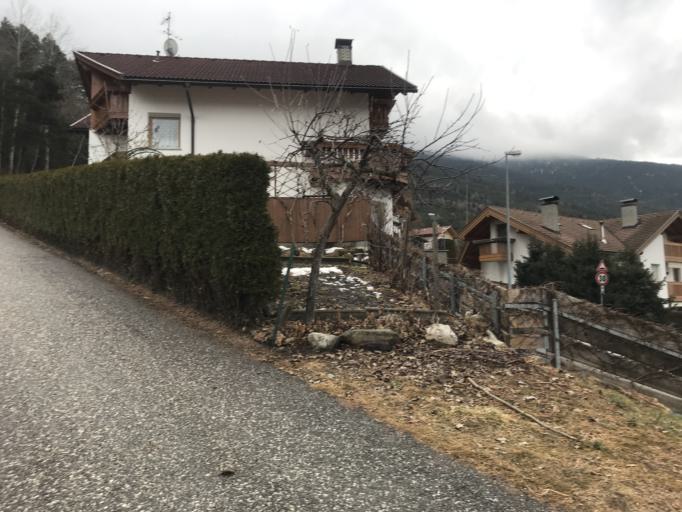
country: IT
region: Trentino-Alto Adige
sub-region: Bolzano
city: Bressanone
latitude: 46.6979
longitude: 11.6789
